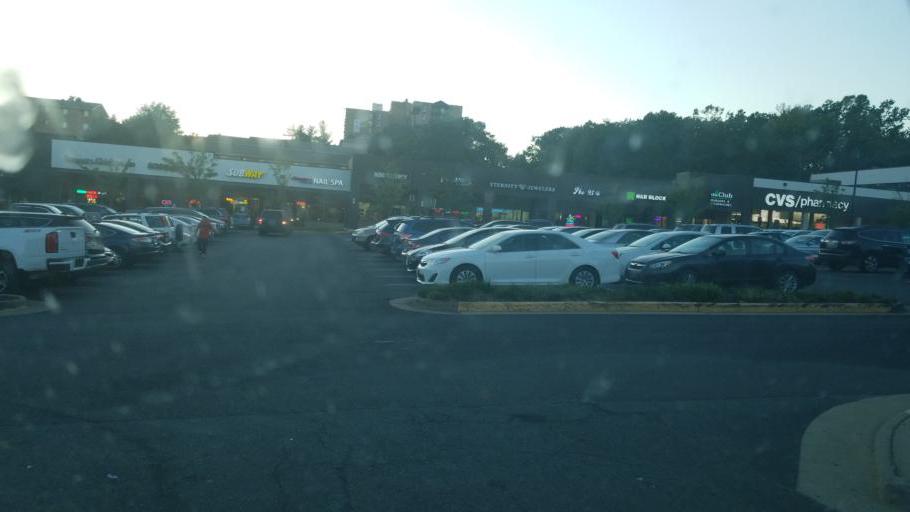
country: US
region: Virginia
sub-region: Fairfax County
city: Lincolnia
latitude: 38.8109
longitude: -77.1327
